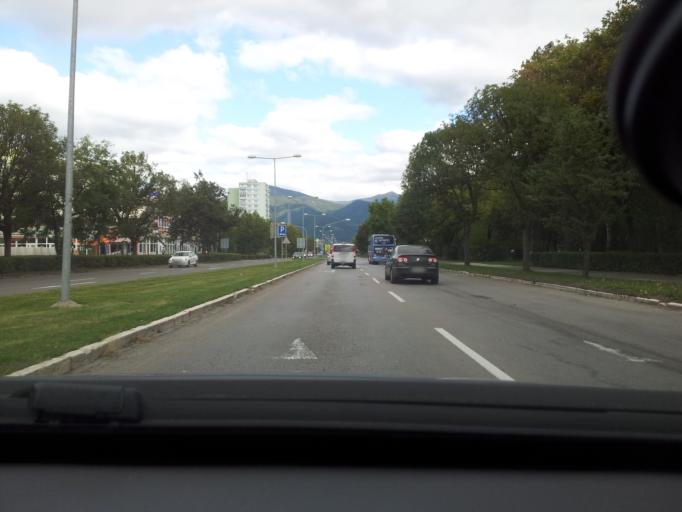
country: SK
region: Zilinsky
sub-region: Okres Martin
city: Martin
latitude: 49.0792
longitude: 18.9288
